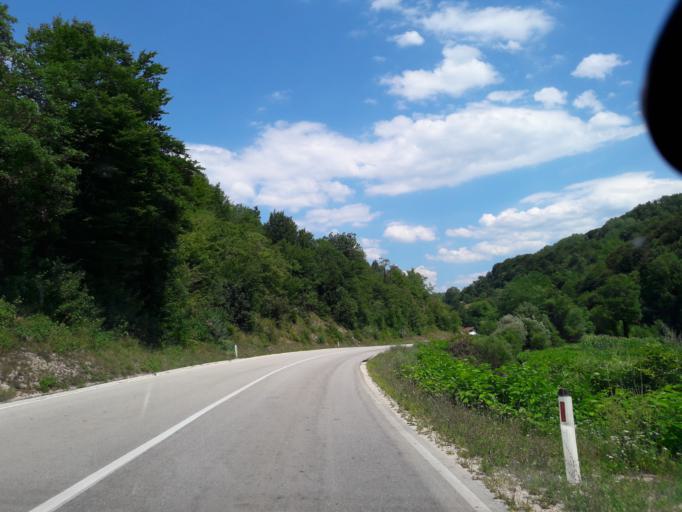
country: BA
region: Republika Srpska
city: Mrkonjic Grad
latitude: 44.4247
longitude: 17.1295
